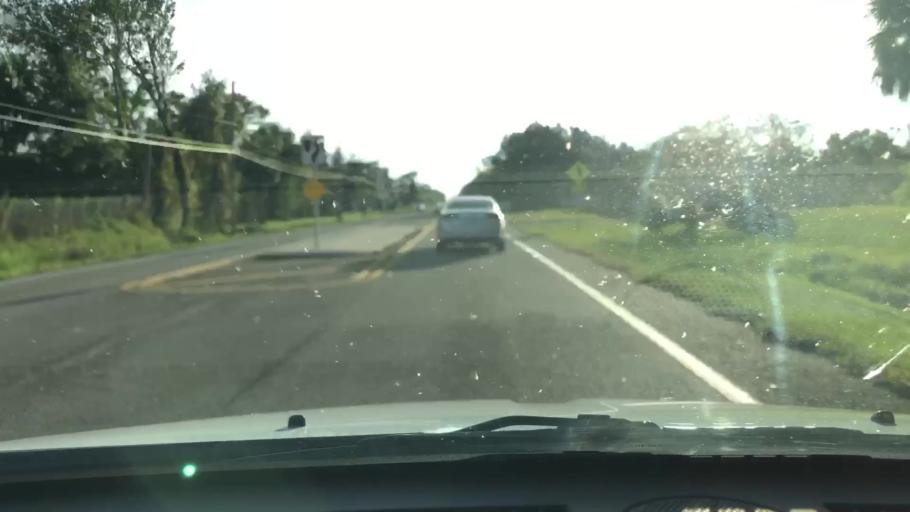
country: US
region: Florida
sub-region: Osceola County
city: Campbell
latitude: 28.2614
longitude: -81.5123
